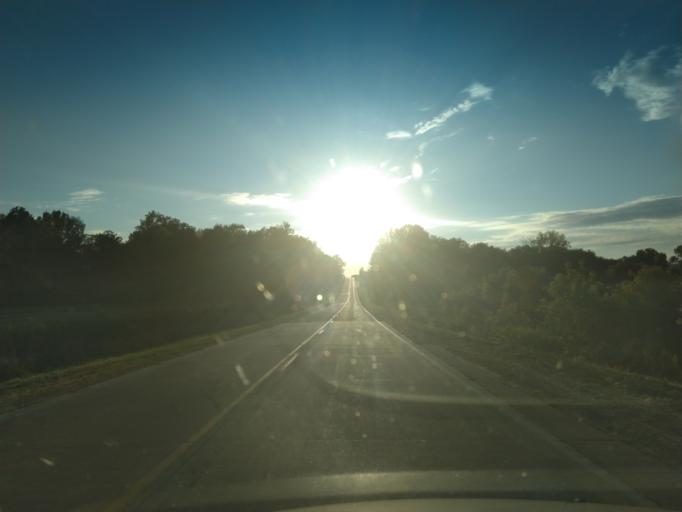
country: US
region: Iowa
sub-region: Jackson County
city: Maquoketa
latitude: 42.1640
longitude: -90.6767
